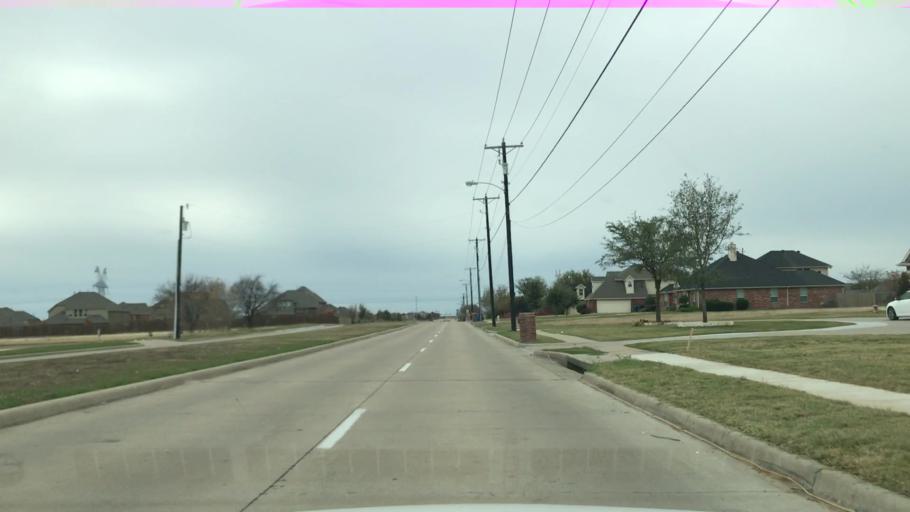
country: US
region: Texas
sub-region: Dallas County
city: Sachse
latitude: 32.9720
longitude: -96.5834
